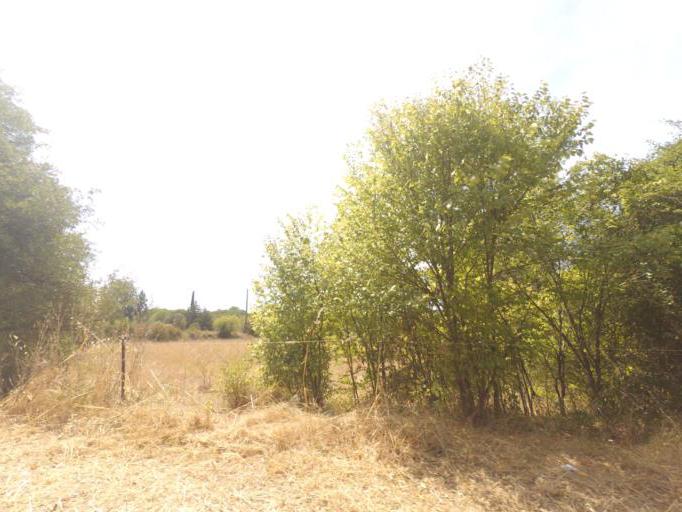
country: FR
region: Languedoc-Roussillon
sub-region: Departement du Gard
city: Aubais
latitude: 43.7690
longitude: 4.1303
